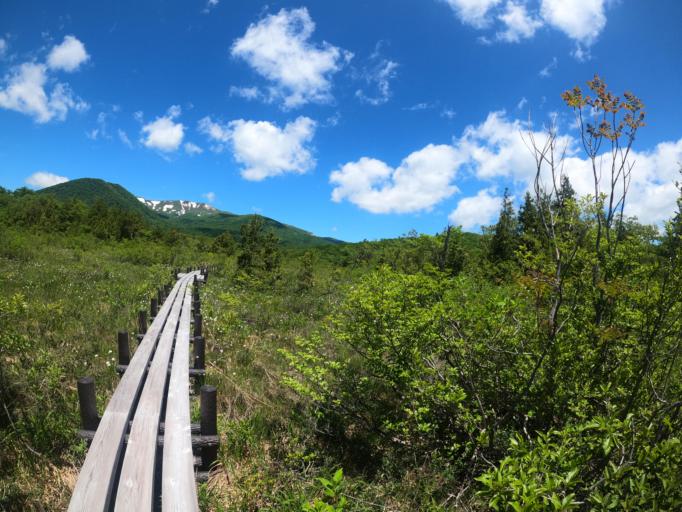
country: JP
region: Iwate
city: Ichinoseki
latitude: 38.9144
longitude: 140.8035
